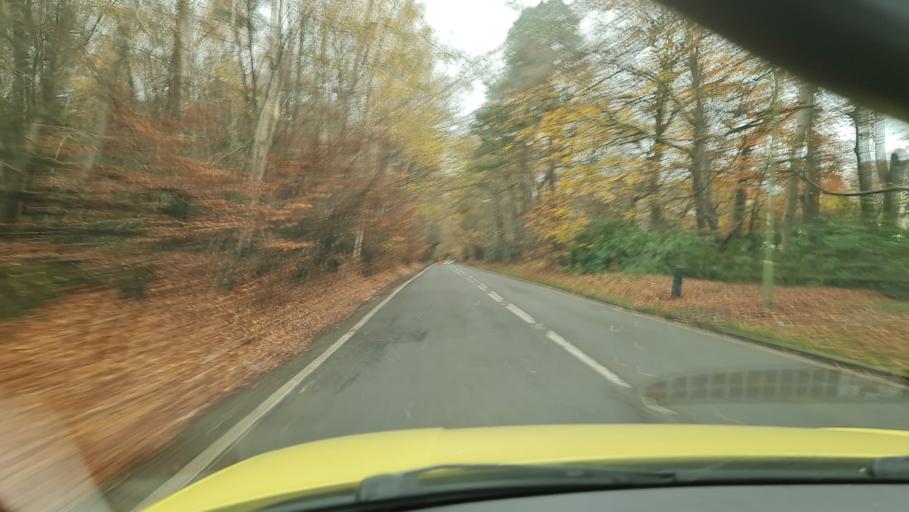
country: GB
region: England
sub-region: Bracknell Forest
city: Sandhurst
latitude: 51.3222
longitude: -0.7813
